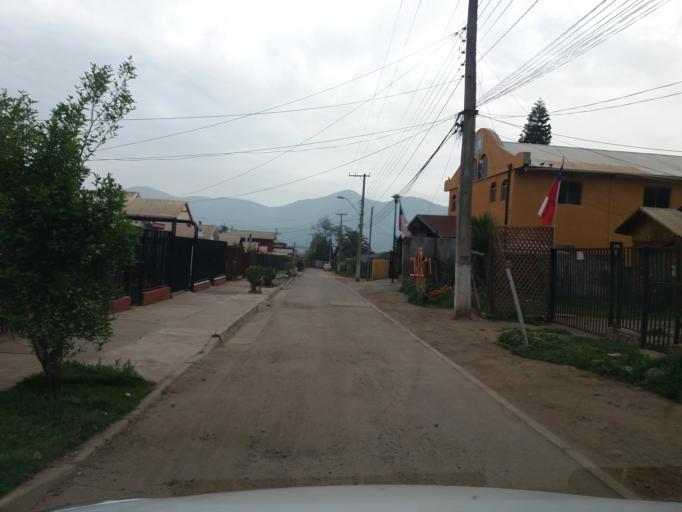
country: CL
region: Valparaiso
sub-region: Provincia de Quillota
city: Hacienda La Calera
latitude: -32.8196
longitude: -71.1319
